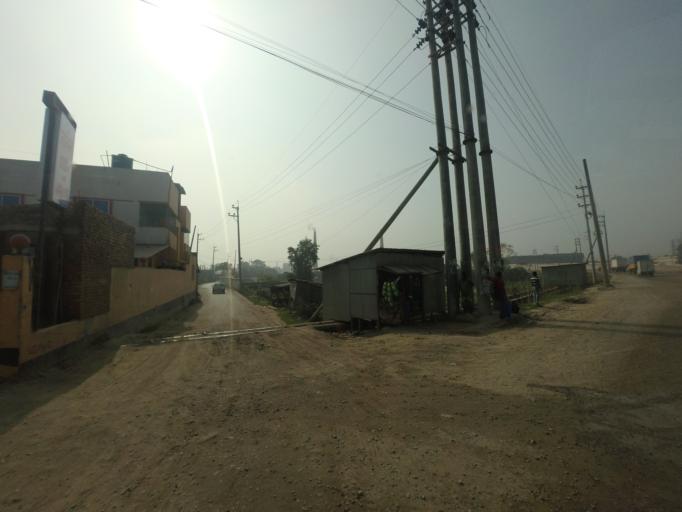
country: BD
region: Dhaka
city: Paltan
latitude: 23.7889
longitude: 90.5686
